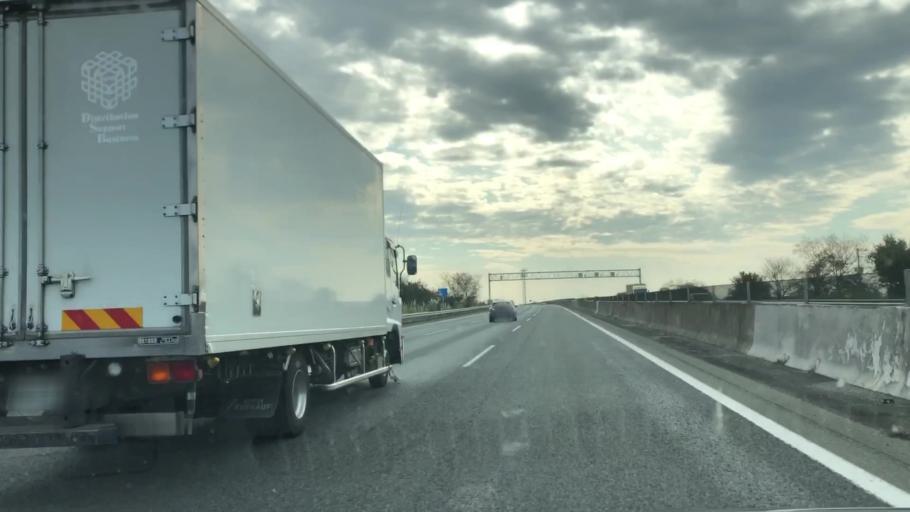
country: JP
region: Saga Prefecture
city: Tosu
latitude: 33.3581
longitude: 130.5395
